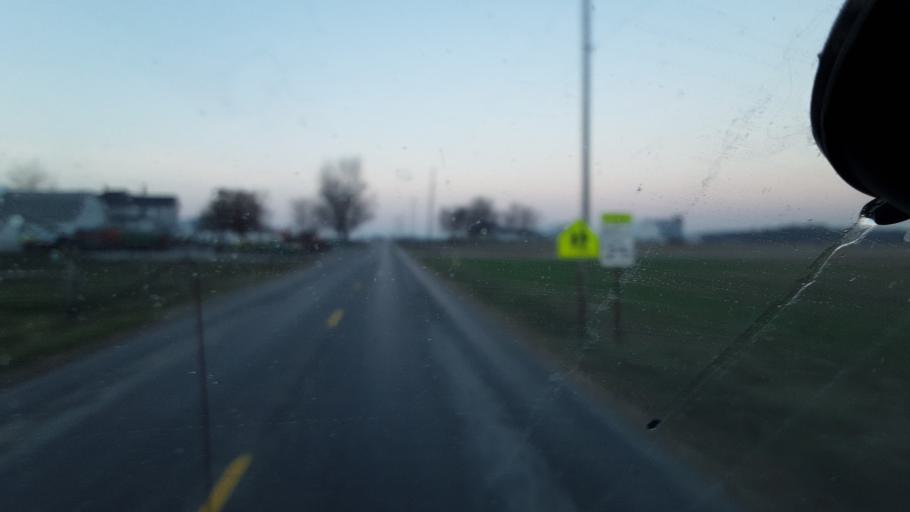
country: US
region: Indiana
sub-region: Allen County
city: Grabill
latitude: 41.2222
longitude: -84.9422
